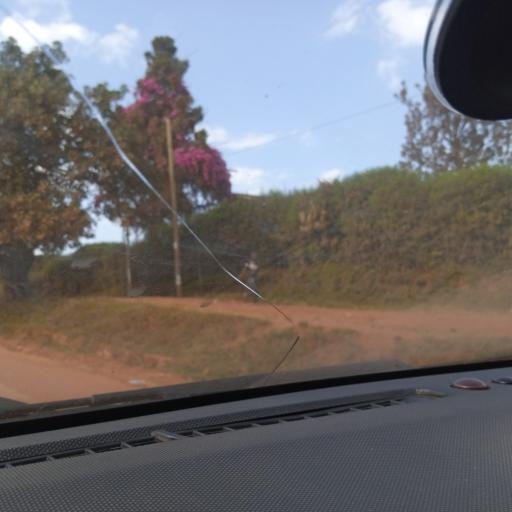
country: UG
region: Central Region
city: Masaka
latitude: -0.3530
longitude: 31.7411
